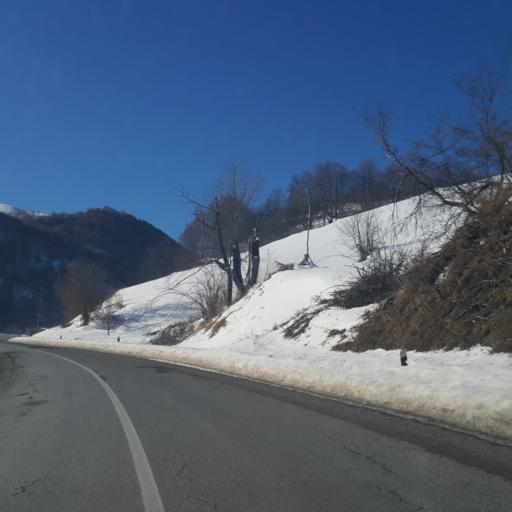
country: RS
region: Central Serbia
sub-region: Rasinski Okrug
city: Aleksandrovac
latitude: 43.3094
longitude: 20.9077
